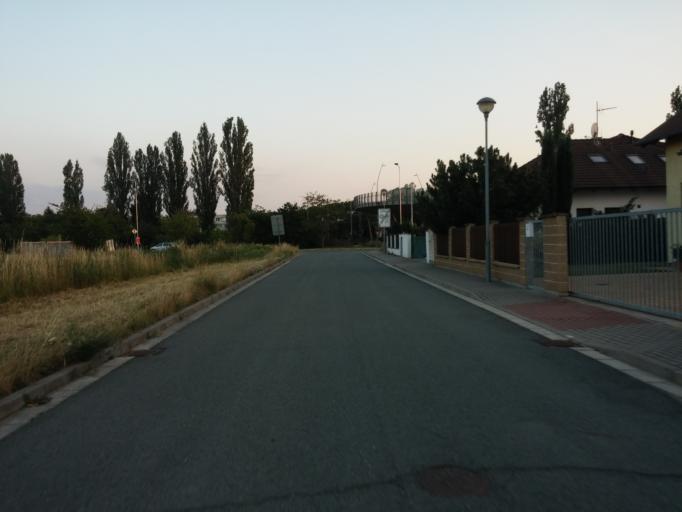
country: CZ
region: Central Bohemia
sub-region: Okres Nymburk
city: Podebrady
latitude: 50.1524
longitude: 15.1224
